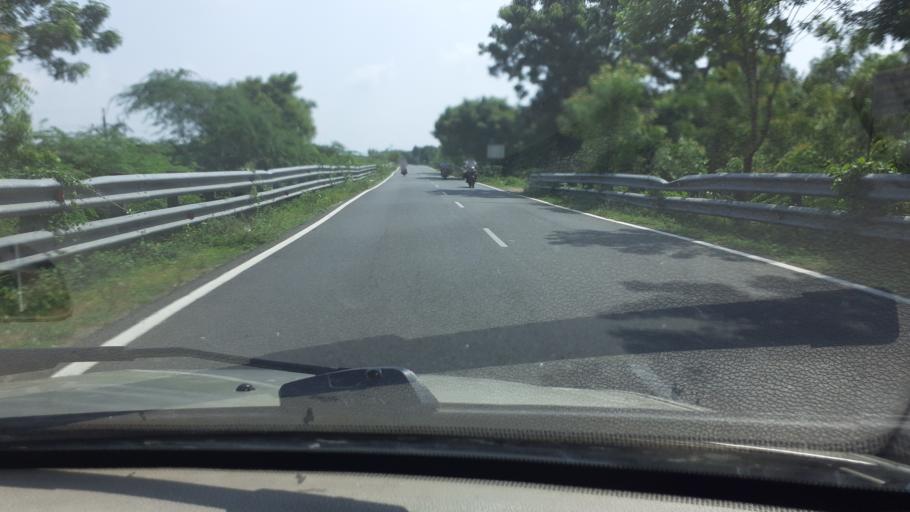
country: IN
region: Tamil Nadu
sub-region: Thoothukkudi
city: Srivaikuntam
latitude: 8.6165
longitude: 77.9152
